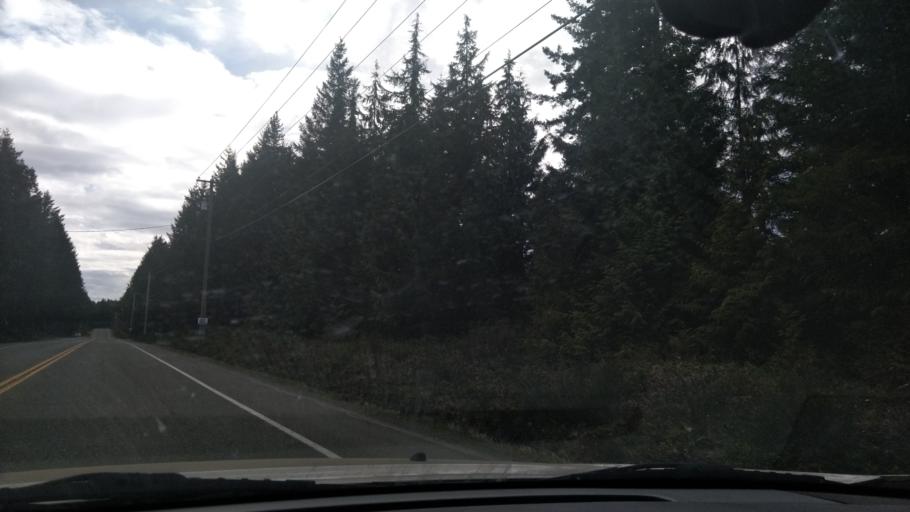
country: CA
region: British Columbia
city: Campbell River
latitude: 50.0162
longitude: -125.3546
